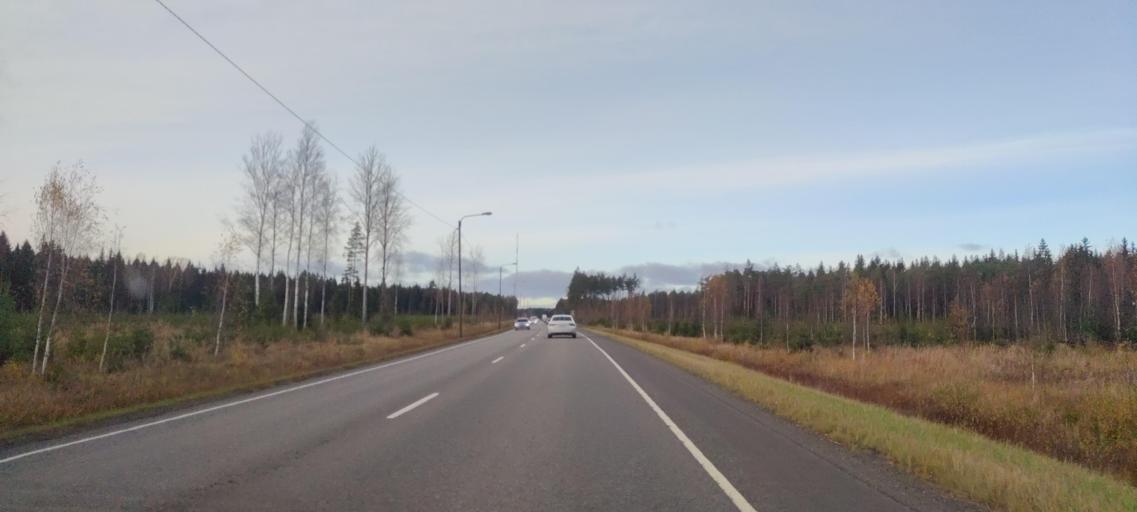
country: FI
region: Satakunta
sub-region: Rauma
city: Eurajoki
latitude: 61.2557
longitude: 21.7102
